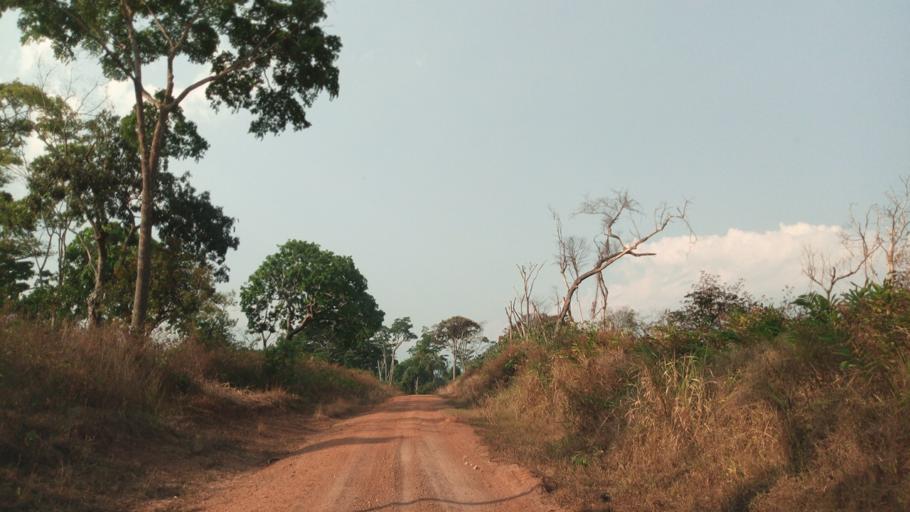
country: CD
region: Katanga
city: Kalemie
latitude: -5.2038
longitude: 28.8699
